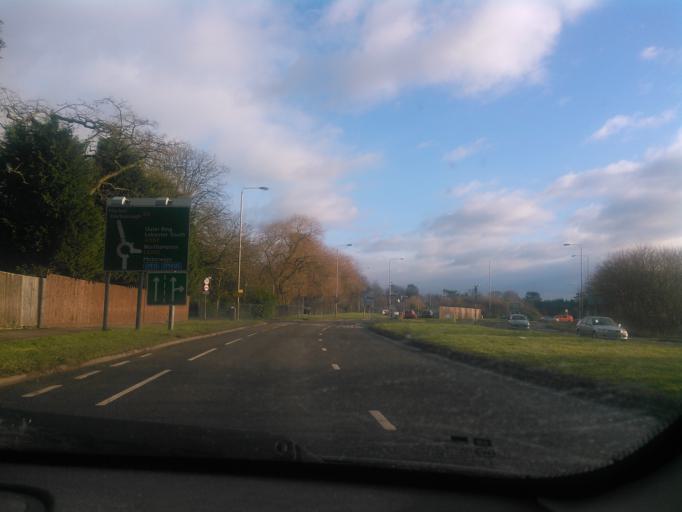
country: GB
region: England
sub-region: Leicestershire
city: Oadby
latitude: 52.6072
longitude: -1.0948
